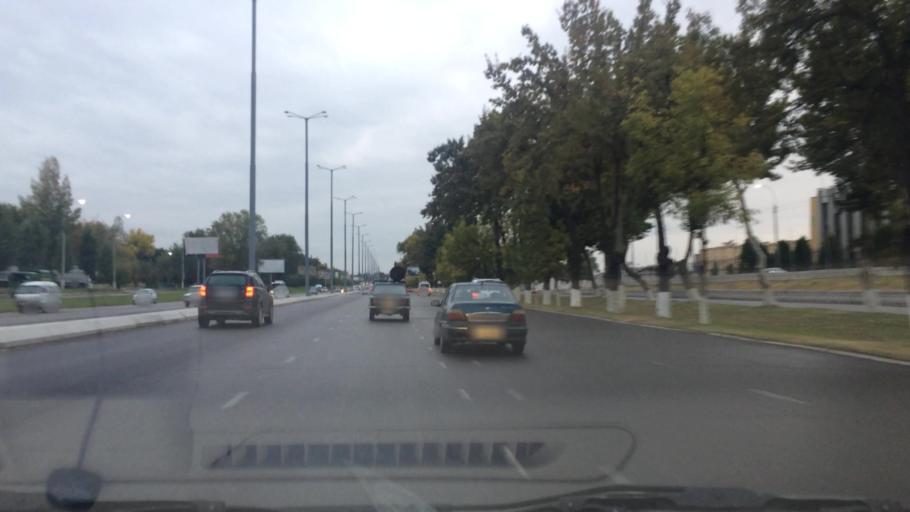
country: UZ
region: Toshkent Shahri
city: Tashkent
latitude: 41.2513
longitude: 69.1846
